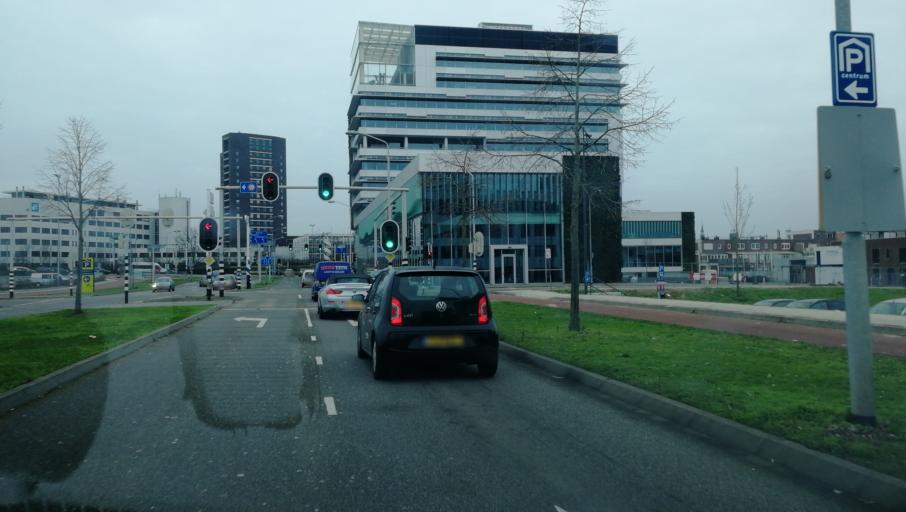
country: NL
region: Limburg
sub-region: Gemeente Venlo
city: Venlo
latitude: 51.3666
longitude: 6.1624
